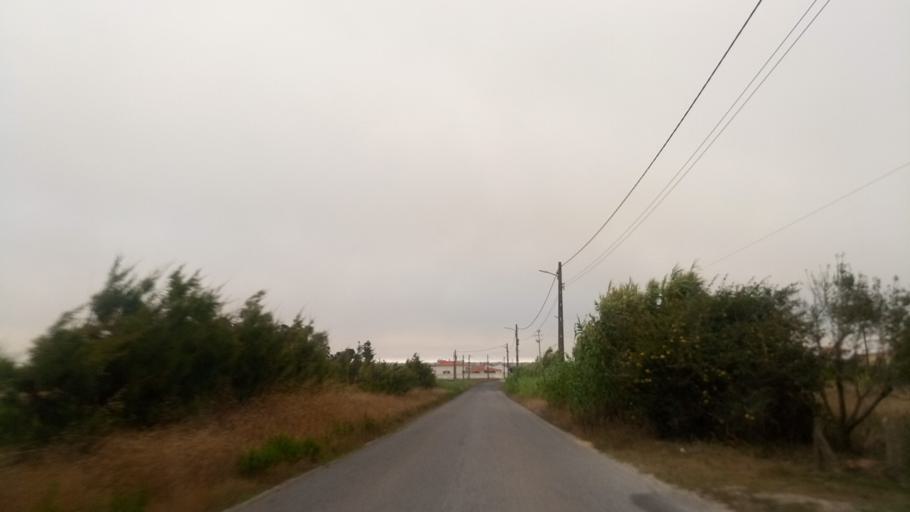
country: PT
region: Leiria
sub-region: Caldas da Rainha
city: Caldas da Rainha
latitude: 39.4405
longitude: -9.1583
